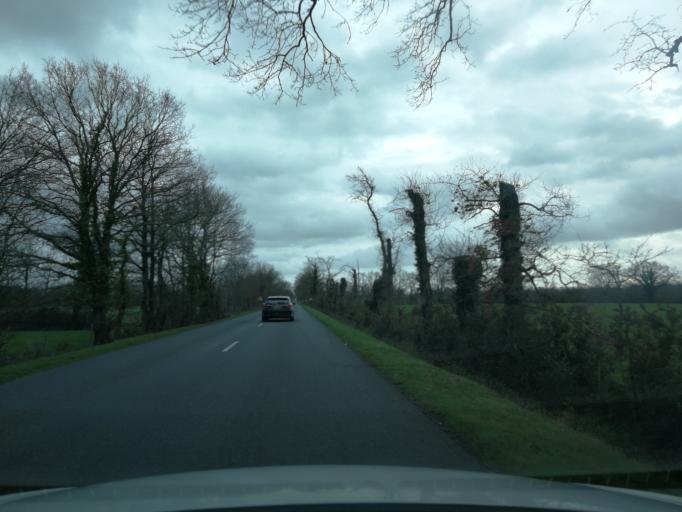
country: FR
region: Pays de la Loire
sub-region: Departement de la Loire-Atlantique
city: Montbert
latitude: 47.0206
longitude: -1.4890
